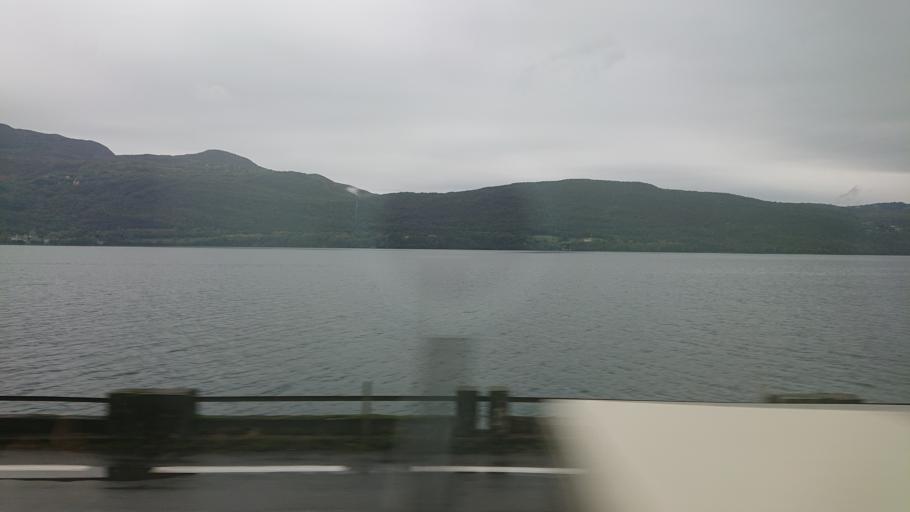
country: FR
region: Rhone-Alpes
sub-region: Departement de la Savoie
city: Chatillon
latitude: 45.7774
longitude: 5.8653
